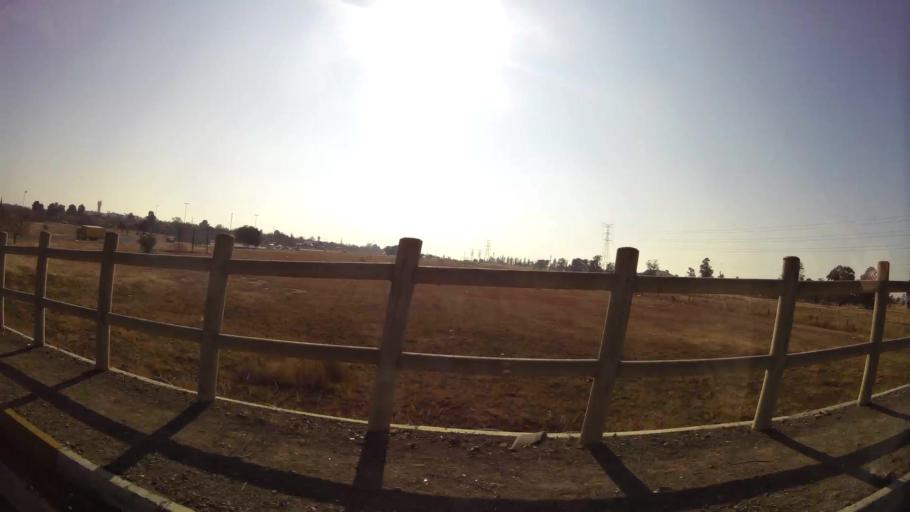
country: ZA
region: Orange Free State
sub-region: Mangaung Metropolitan Municipality
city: Bloemfontein
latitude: -29.1712
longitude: 26.1950
